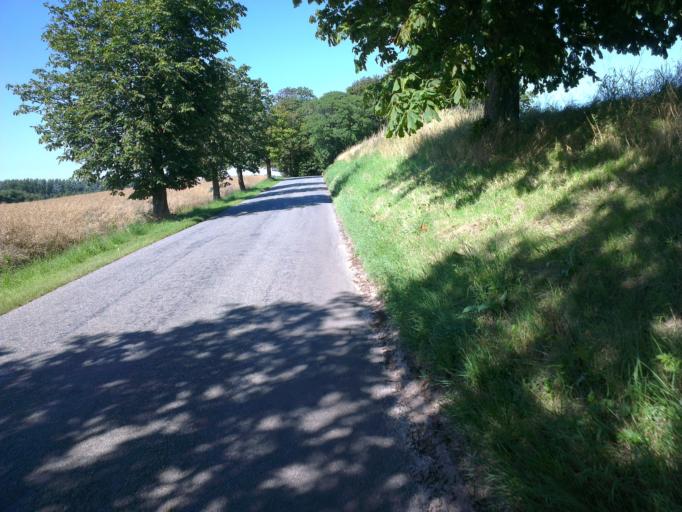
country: DK
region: Capital Region
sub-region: Frederikssund Kommune
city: Skibby
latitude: 55.7215
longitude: 11.9522
